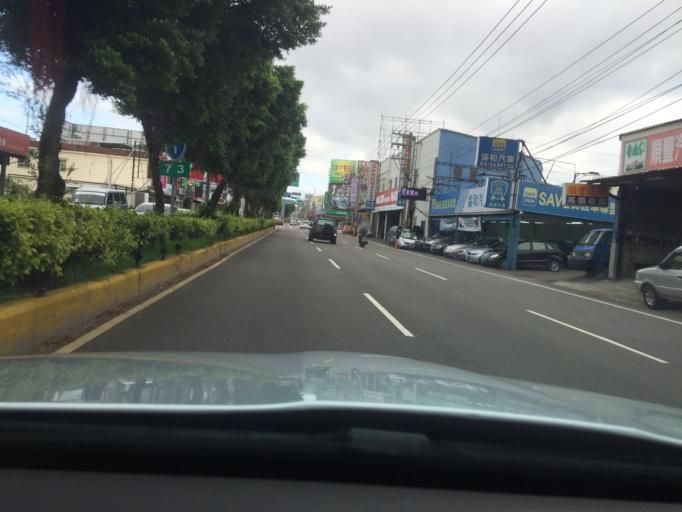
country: TW
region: Taiwan
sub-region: Hsinchu
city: Hsinchu
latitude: 24.8149
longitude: 120.9839
